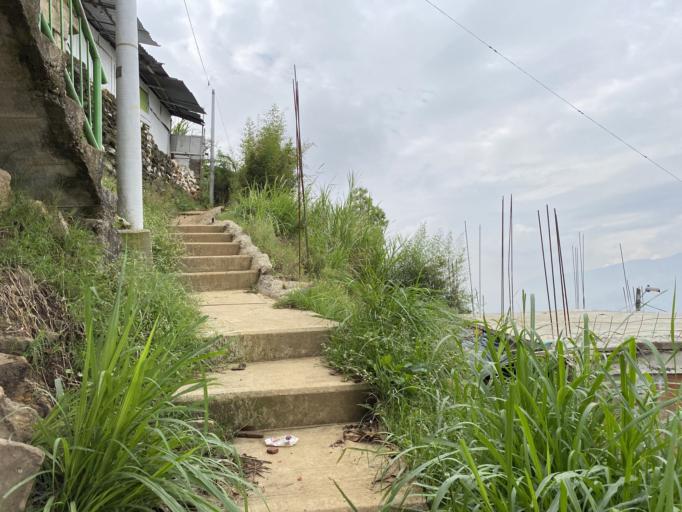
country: CO
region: Antioquia
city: Medellin
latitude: 6.2621
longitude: -75.5405
